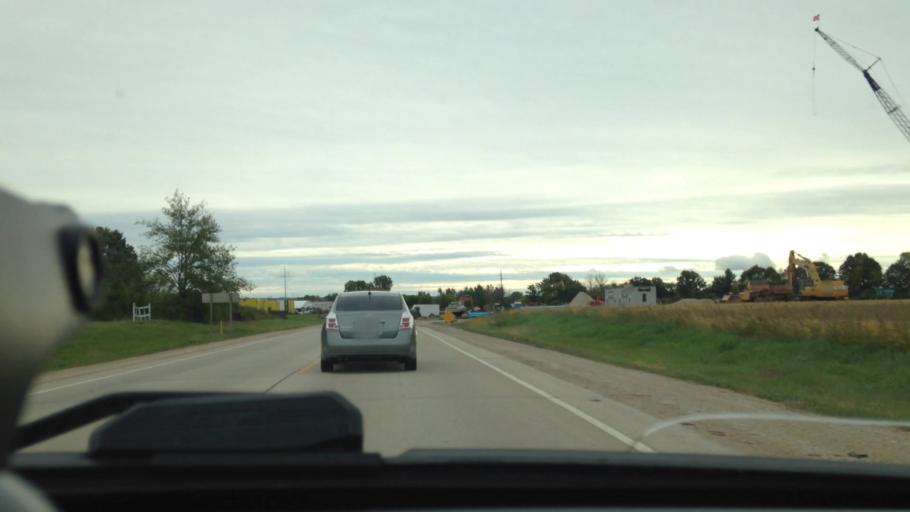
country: US
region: Wisconsin
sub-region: Fond du Lac County
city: North Fond du Lac
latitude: 43.7985
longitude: -88.4915
